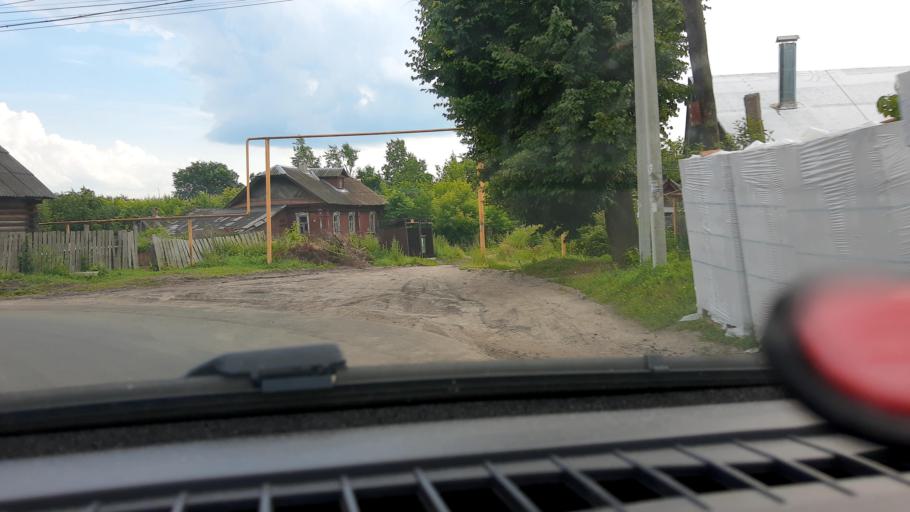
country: RU
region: Nizjnij Novgorod
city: Gorodets
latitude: 56.6231
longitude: 43.4780
